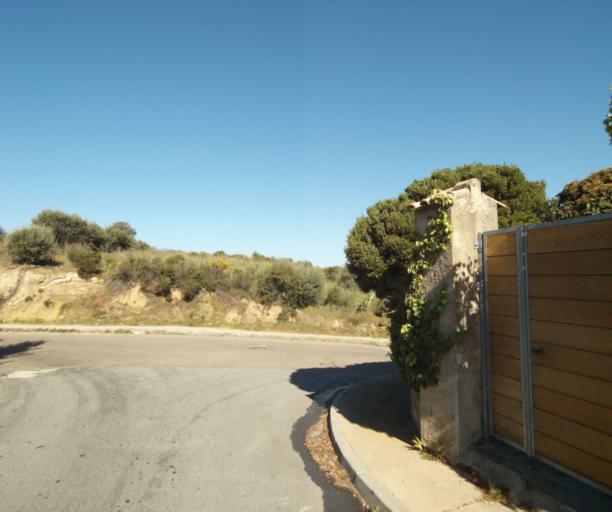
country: FR
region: Corsica
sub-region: Departement de la Corse-du-Sud
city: Propriano
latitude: 41.6700
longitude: 8.8976
